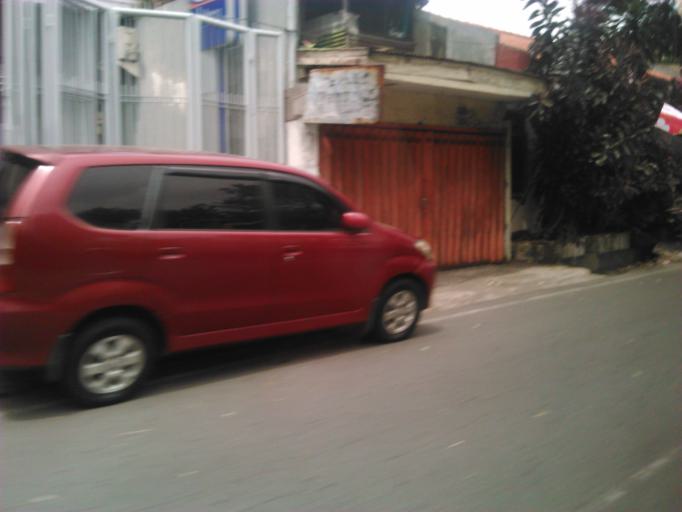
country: ID
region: East Java
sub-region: Kota Surabaya
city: Surabaya
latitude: -7.2567
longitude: 112.7276
